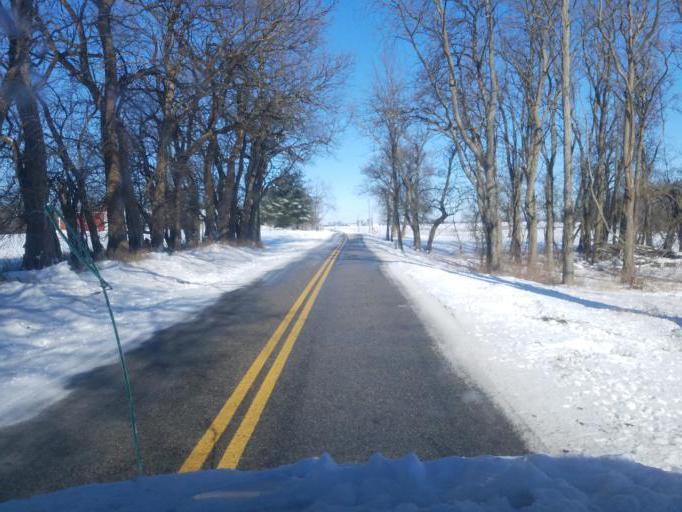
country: US
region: Ohio
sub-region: Delaware County
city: Delaware
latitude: 40.3027
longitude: -82.9887
